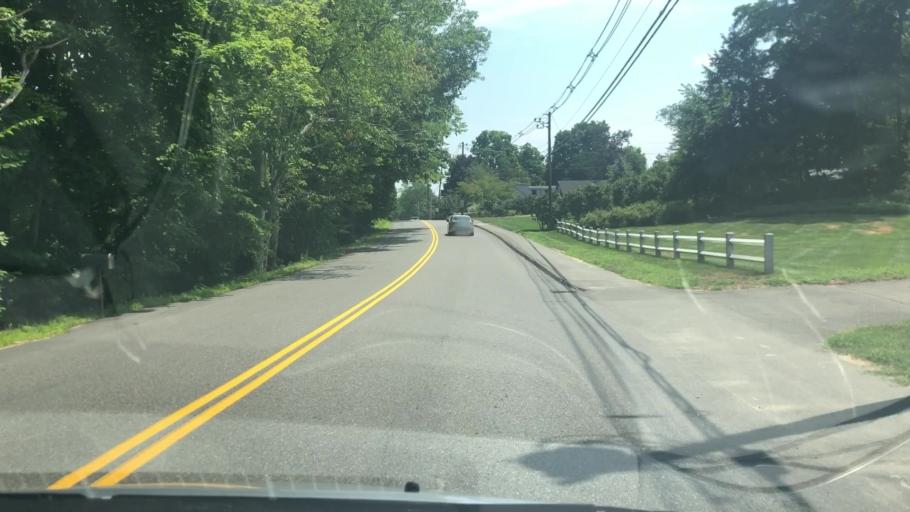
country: US
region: New Hampshire
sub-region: Hillsborough County
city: Milford
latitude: 42.8666
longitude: -71.6305
